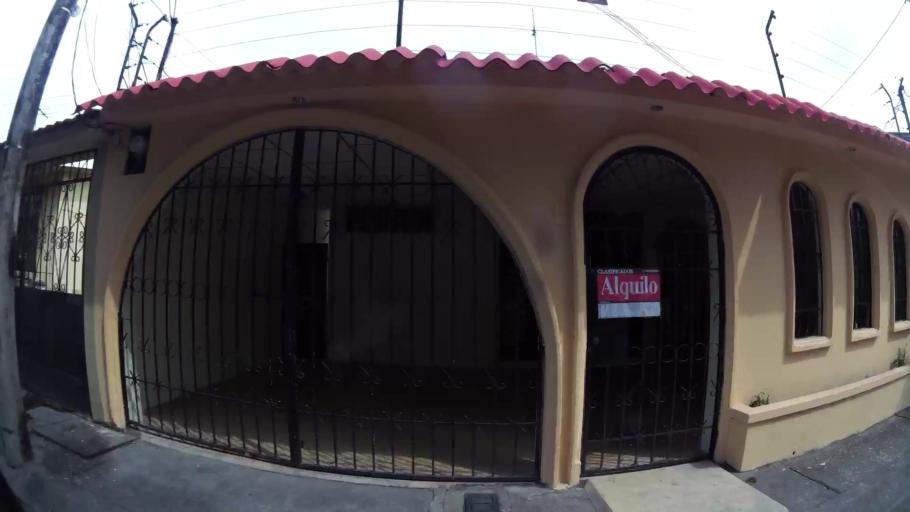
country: EC
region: Guayas
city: Eloy Alfaro
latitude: -2.1183
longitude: -79.8897
